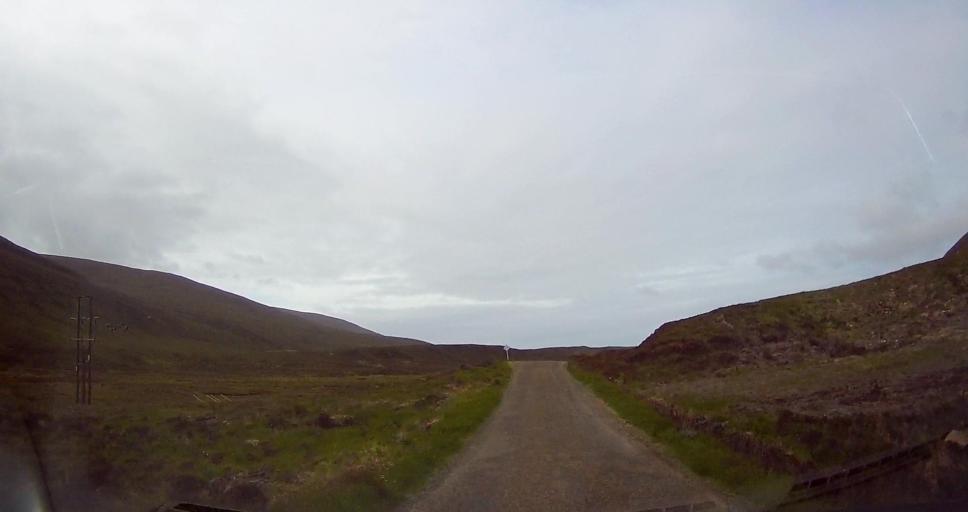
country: GB
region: Scotland
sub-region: Orkney Islands
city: Stromness
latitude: 58.8832
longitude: -3.3392
